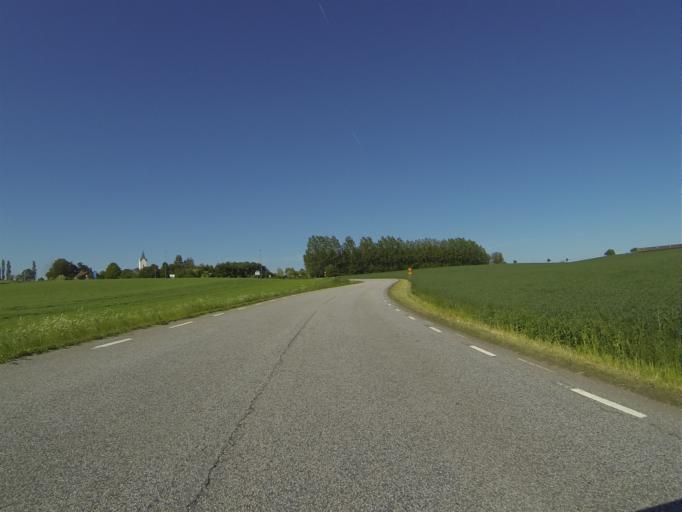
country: SE
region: Skane
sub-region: Staffanstorps Kommun
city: Hjaerup
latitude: 55.6183
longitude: 13.1575
